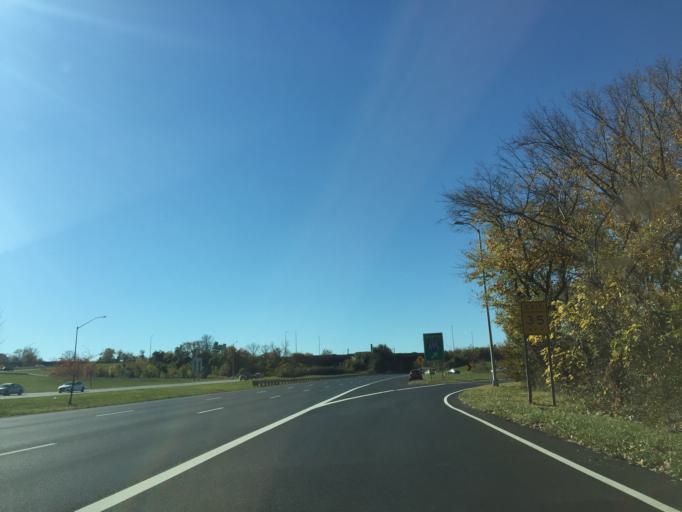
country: US
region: Maryland
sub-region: Anne Arundel County
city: Linthicum
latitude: 39.2209
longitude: -76.6559
